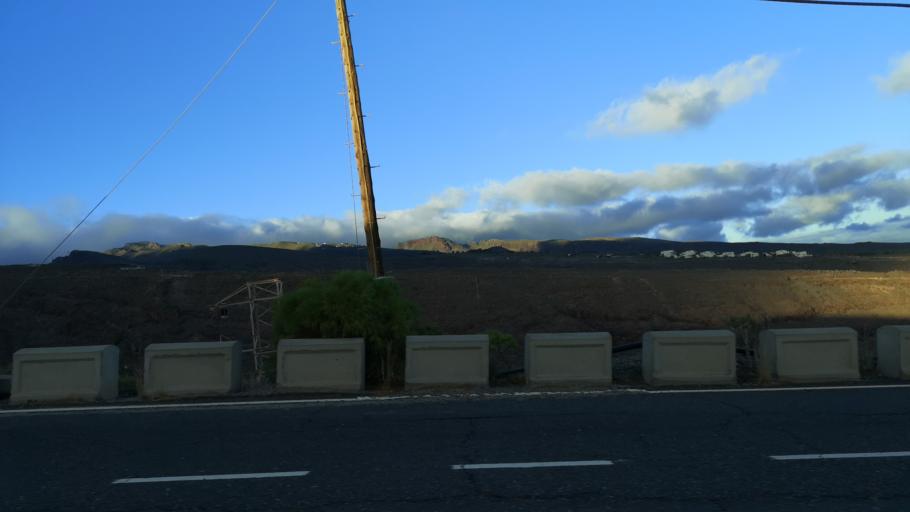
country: ES
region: Canary Islands
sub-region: Provincia de Santa Cruz de Tenerife
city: Alajero
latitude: 28.0322
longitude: -17.2089
